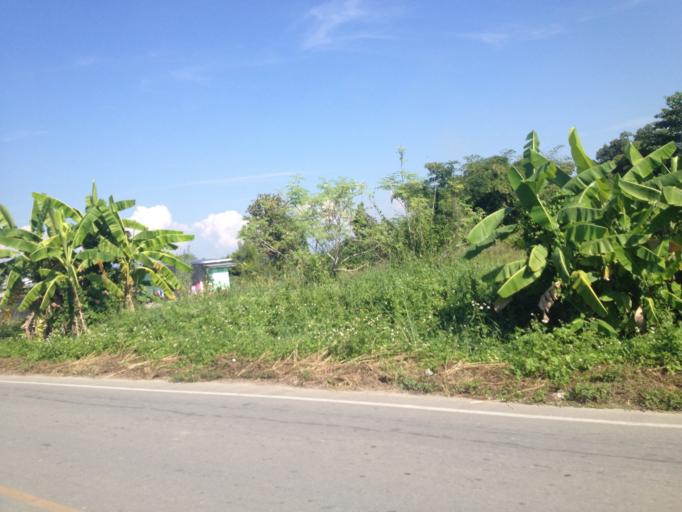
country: TH
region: Chiang Mai
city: Hang Dong
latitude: 18.6930
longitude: 98.9627
